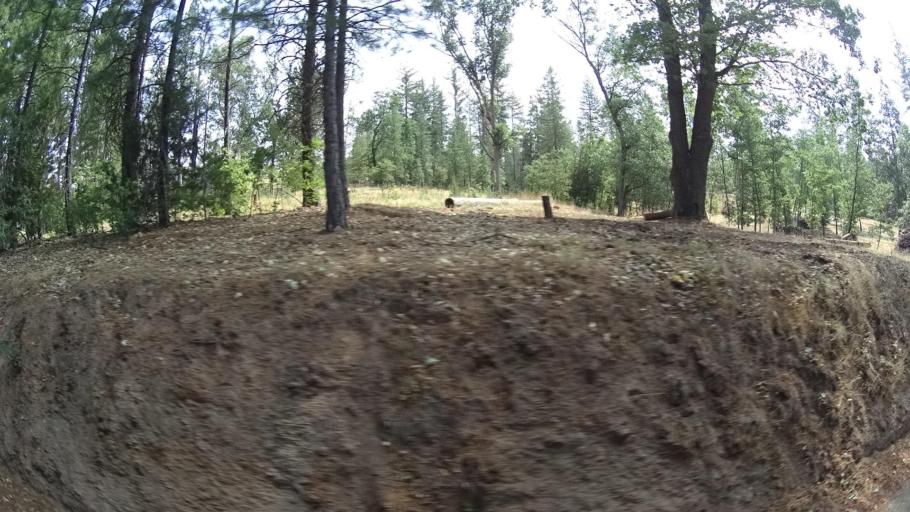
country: US
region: California
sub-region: Tuolumne County
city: Tuolumne City
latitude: 37.7526
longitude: -120.1381
